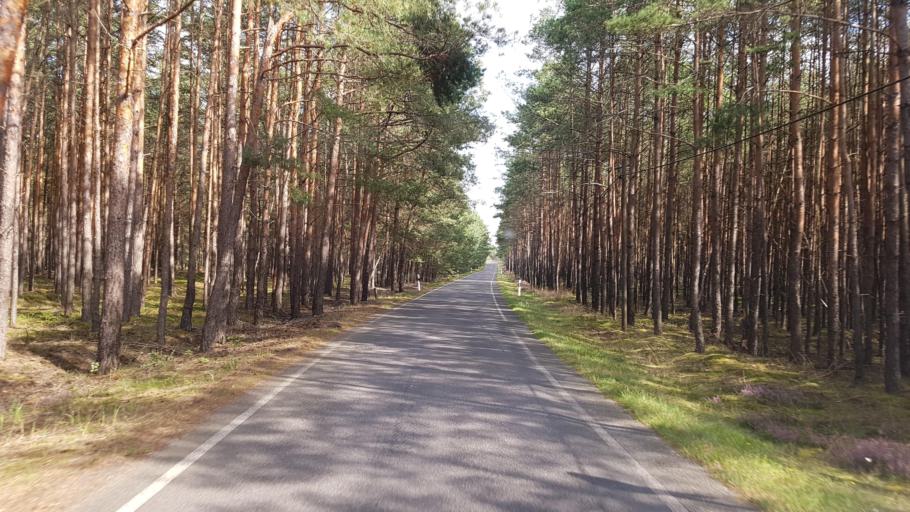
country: DE
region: Brandenburg
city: Schonewalde
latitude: 51.7545
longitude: 13.5793
